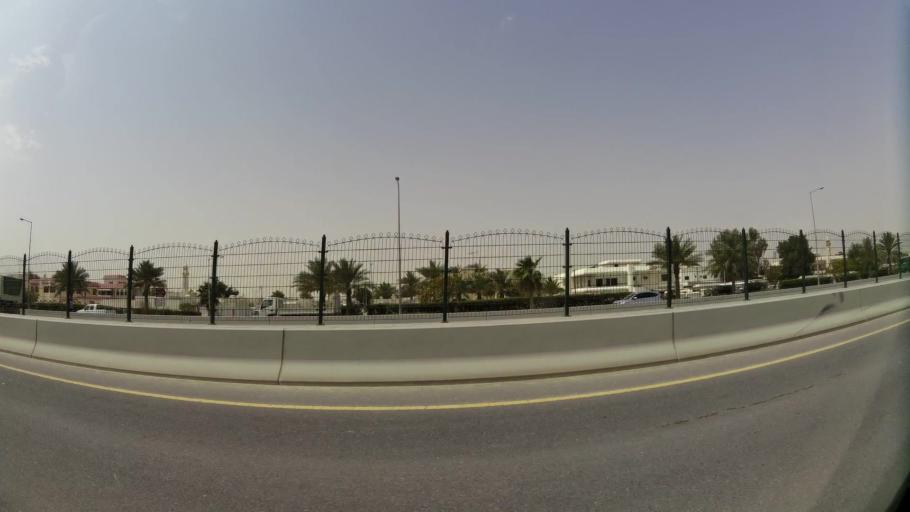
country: QA
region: Baladiyat ar Rayyan
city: Ar Rayyan
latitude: 25.2308
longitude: 51.4312
